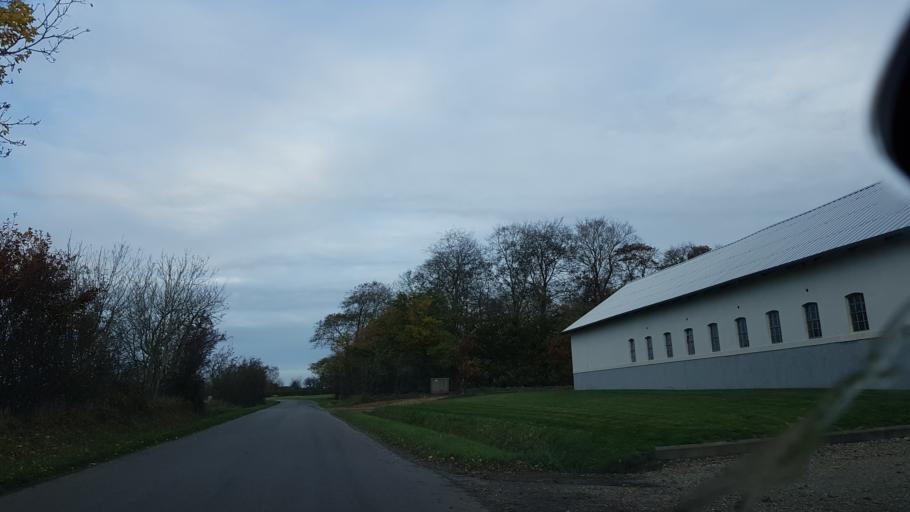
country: DK
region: South Denmark
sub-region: Haderslev Kommune
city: Vojens
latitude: 55.2532
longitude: 9.1922
